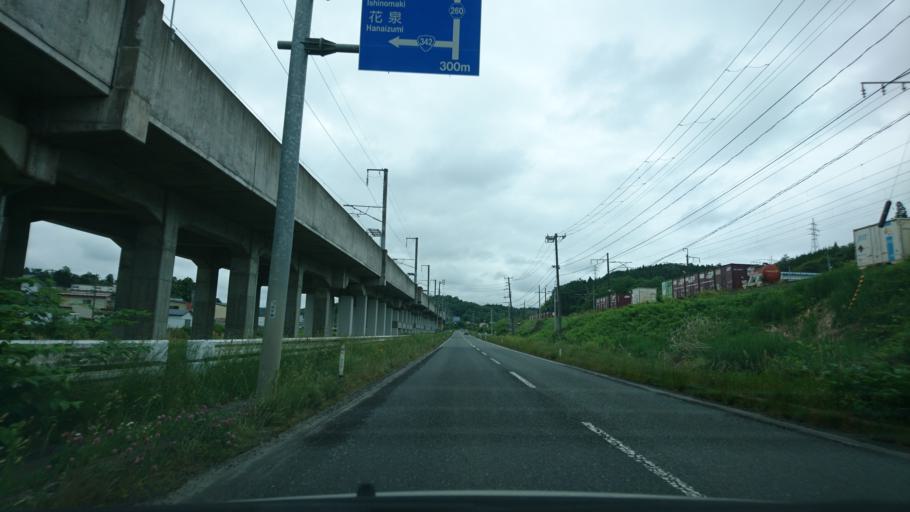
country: JP
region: Iwate
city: Ichinoseki
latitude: 38.9034
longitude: 141.1300
